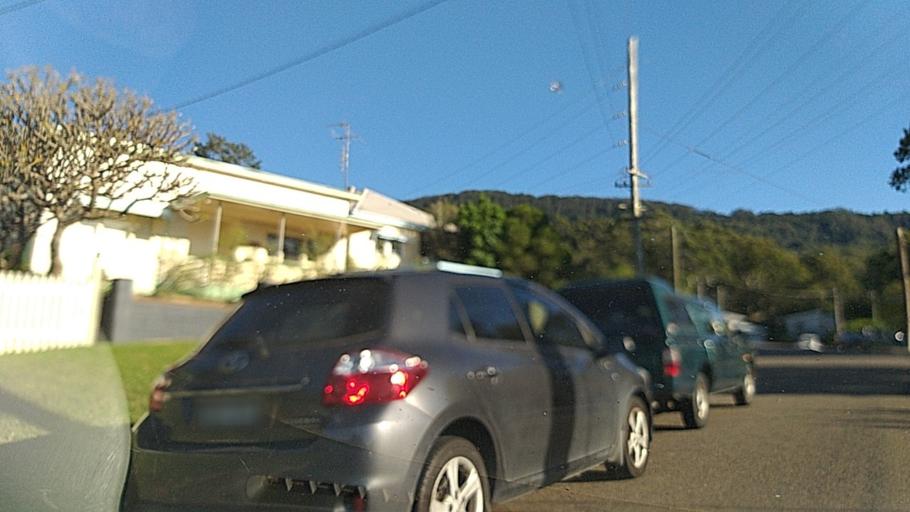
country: AU
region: New South Wales
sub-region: Wollongong
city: Bulli
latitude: -34.3261
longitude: 150.9071
